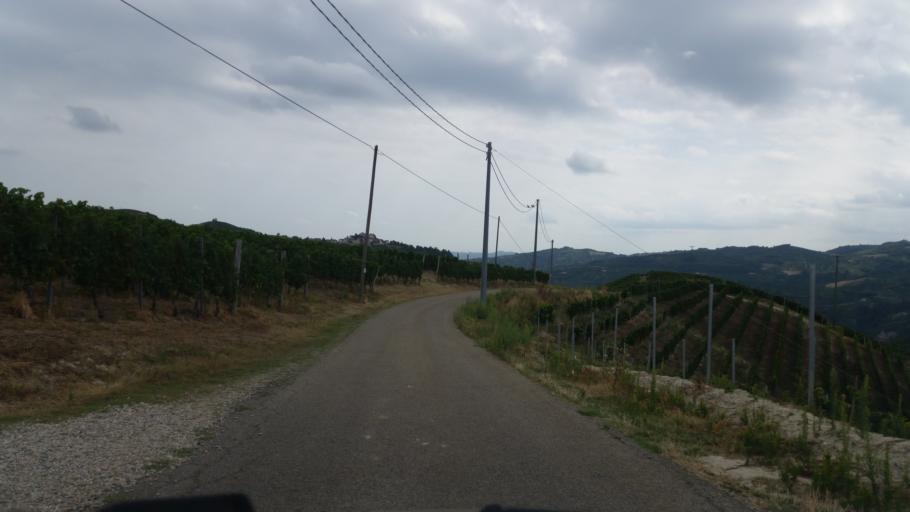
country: IT
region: Piedmont
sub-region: Provincia di Cuneo
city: Mango
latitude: 44.6889
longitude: 8.1702
